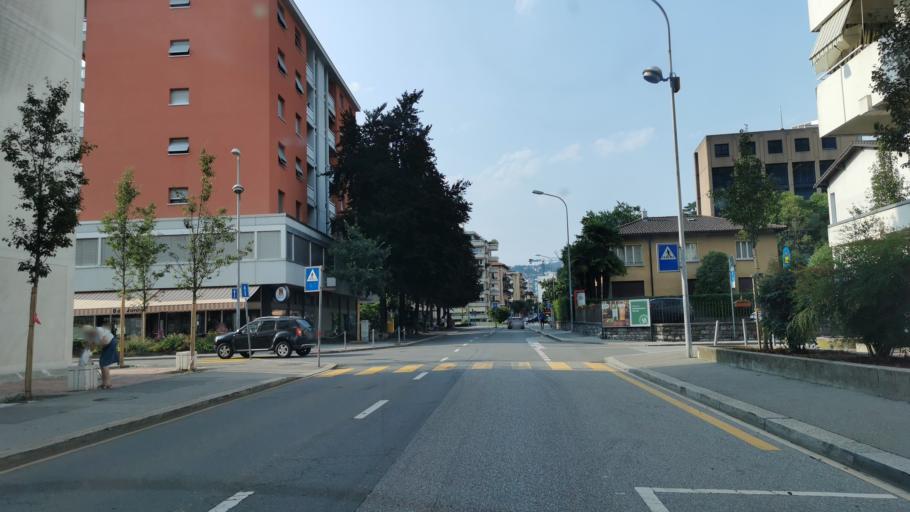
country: CH
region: Ticino
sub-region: Lugano District
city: Lugano
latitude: 46.0083
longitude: 8.9642
